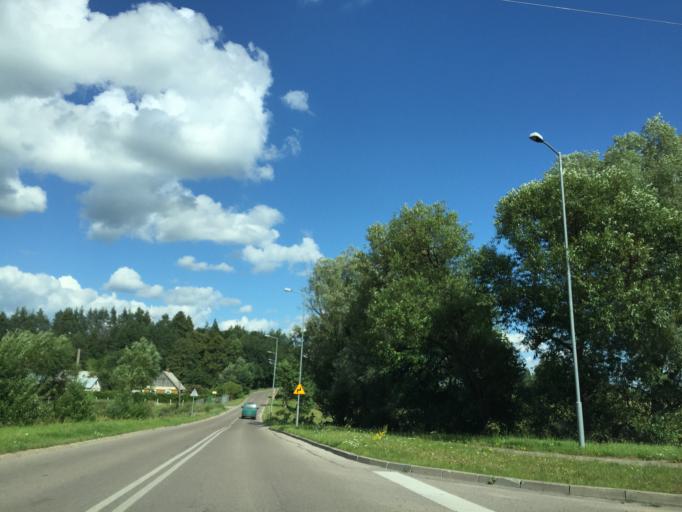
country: PL
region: Podlasie
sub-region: Suwalki
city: Suwalki
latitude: 54.1141
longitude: 22.9654
